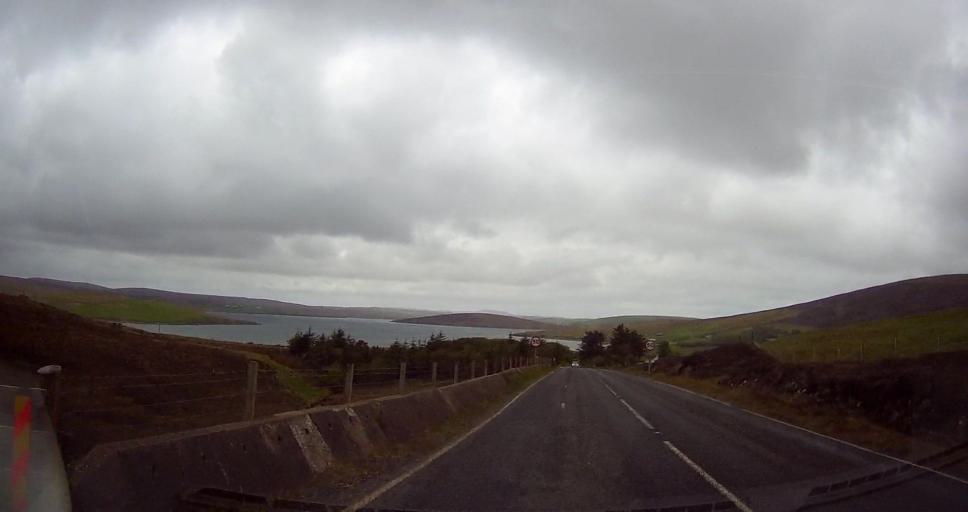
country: GB
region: Scotland
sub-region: Shetland Islands
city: Lerwick
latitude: 60.2410
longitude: -1.3393
